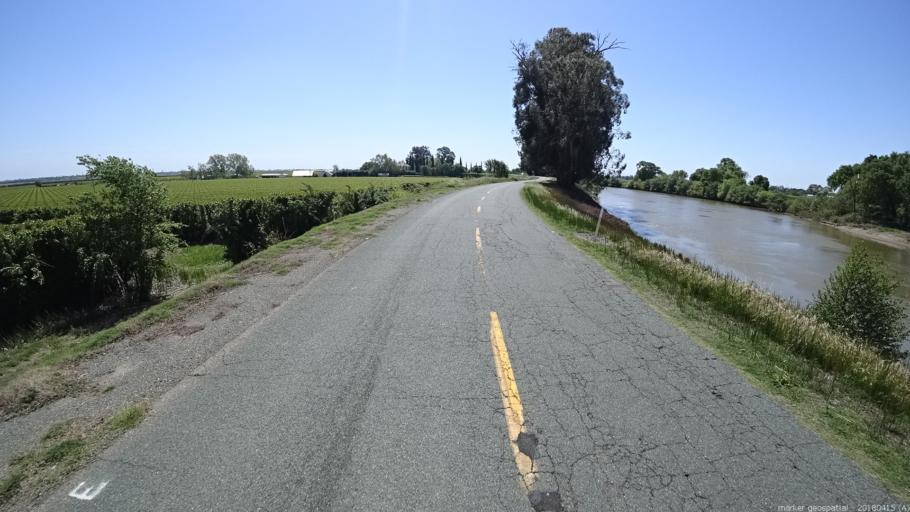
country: US
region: California
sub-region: Sacramento County
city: Walnut Grove
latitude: 38.2732
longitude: -121.5876
